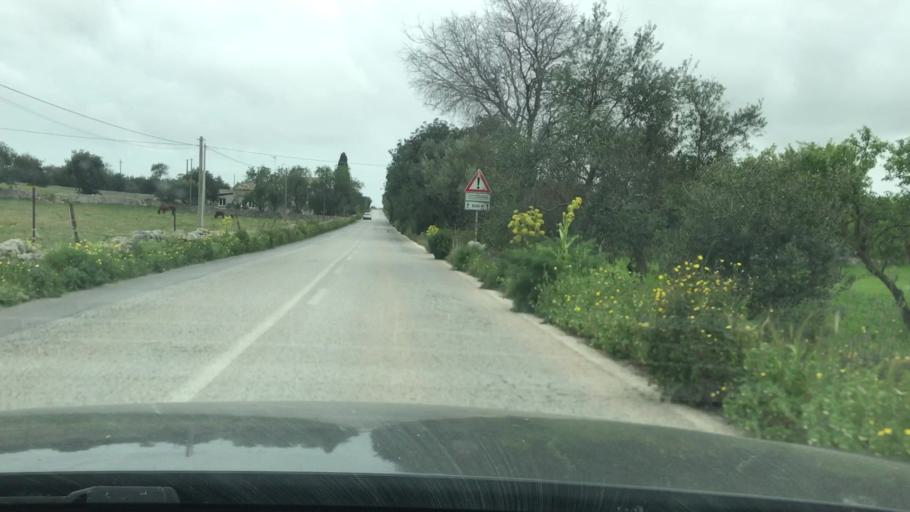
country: IT
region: Sicily
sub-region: Ragusa
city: Scicli
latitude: 36.8118
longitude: 14.7299
